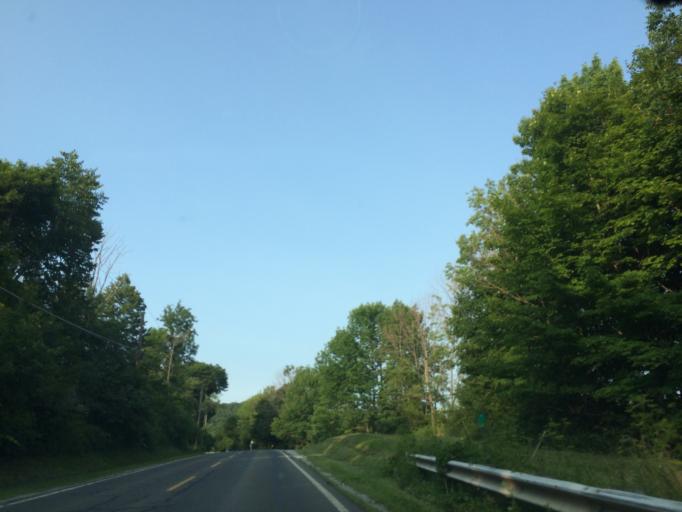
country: US
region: Massachusetts
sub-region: Berkshire County
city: Richmond
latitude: 42.3917
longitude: -73.3903
